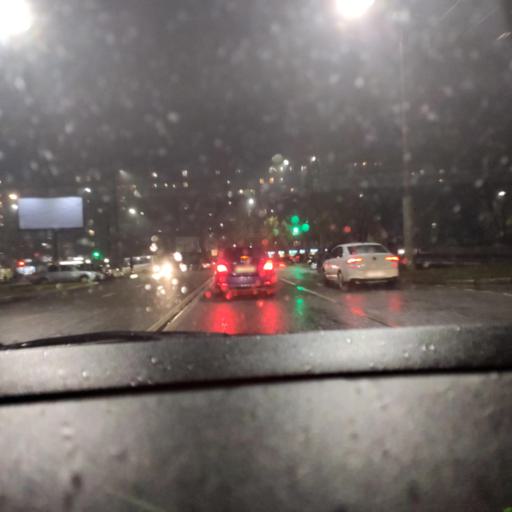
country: RU
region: Voronezj
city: Pridonskoy
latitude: 51.6532
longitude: 39.1214
